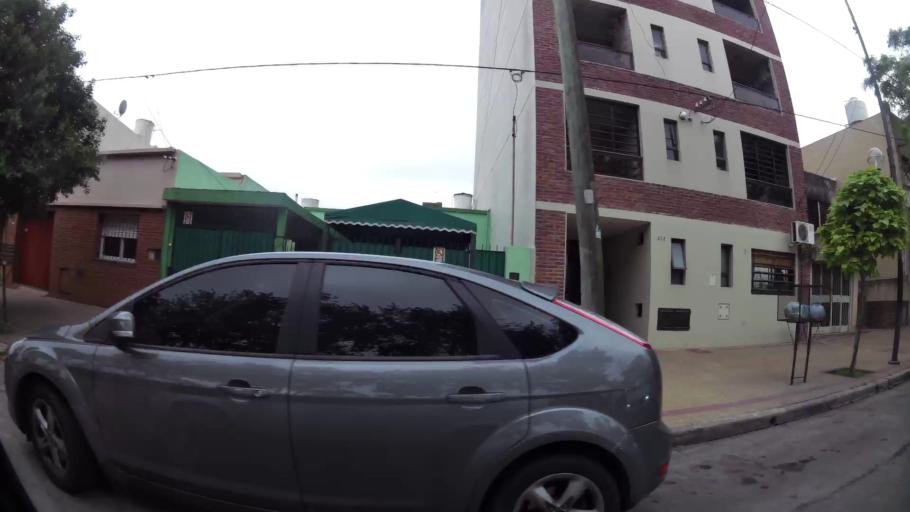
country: AR
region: Buenos Aires
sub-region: Partido de La Plata
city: La Plata
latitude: -34.9211
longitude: -57.9801
